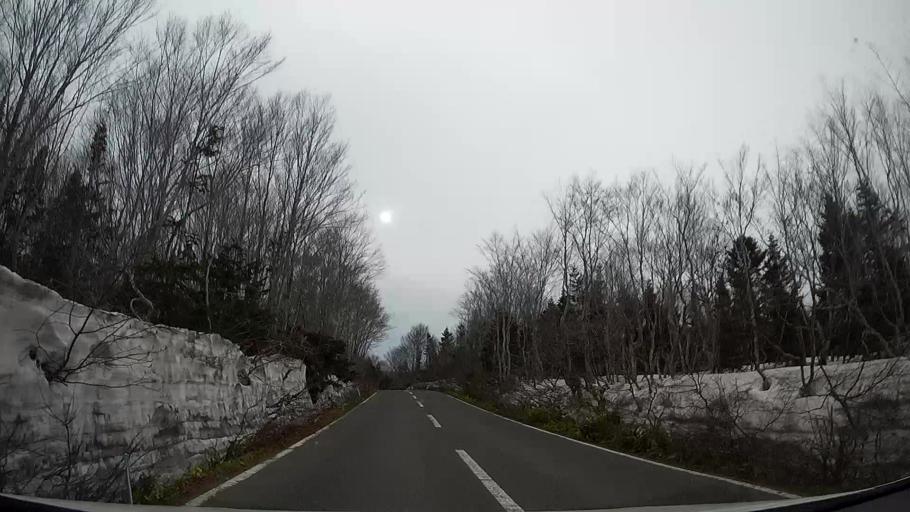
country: JP
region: Aomori
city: Aomori Shi
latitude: 40.6304
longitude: 140.9155
